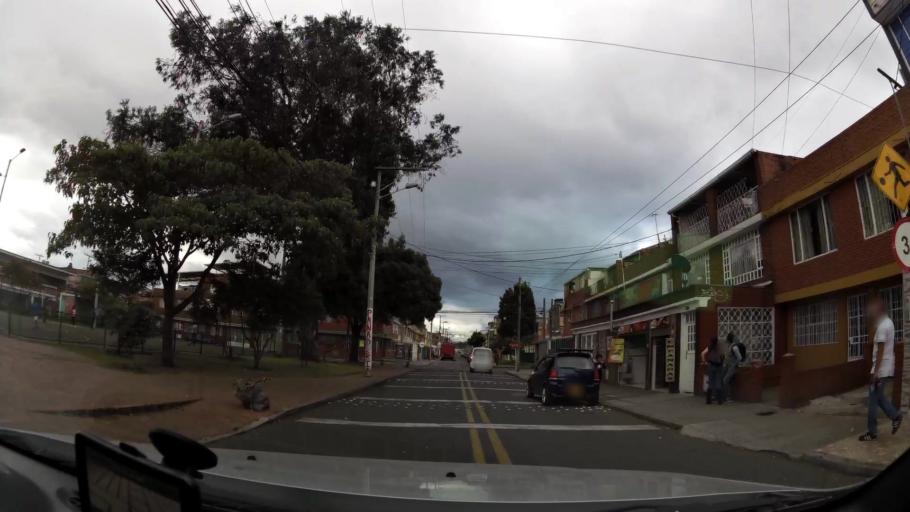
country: CO
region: Bogota D.C.
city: Bogota
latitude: 4.6025
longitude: -74.1088
